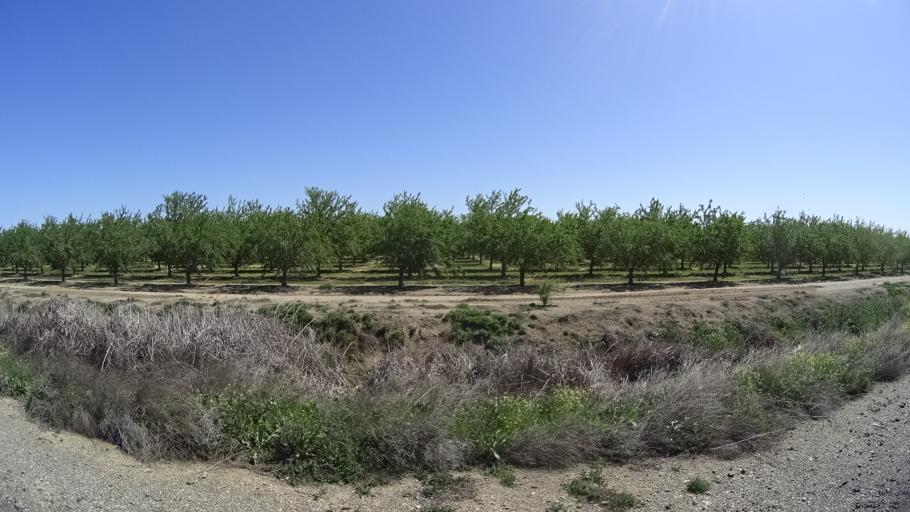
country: US
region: California
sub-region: Glenn County
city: Orland
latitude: 39.6878
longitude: -122.2530
